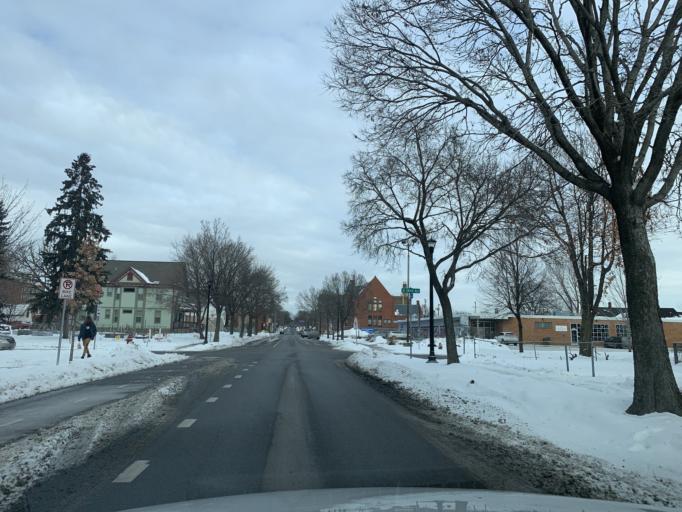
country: US
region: Minnesota
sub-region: Hennepin County
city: Minneapolis
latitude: 44.9970
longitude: -93.2941
